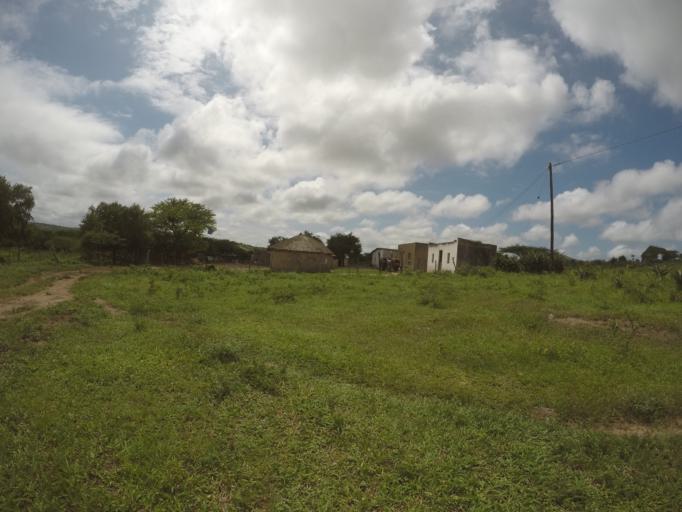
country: ZA
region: KwaZulu-Natal
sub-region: uThungulu District Municipality
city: Empangeni
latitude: -28.5710
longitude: 31.8448
